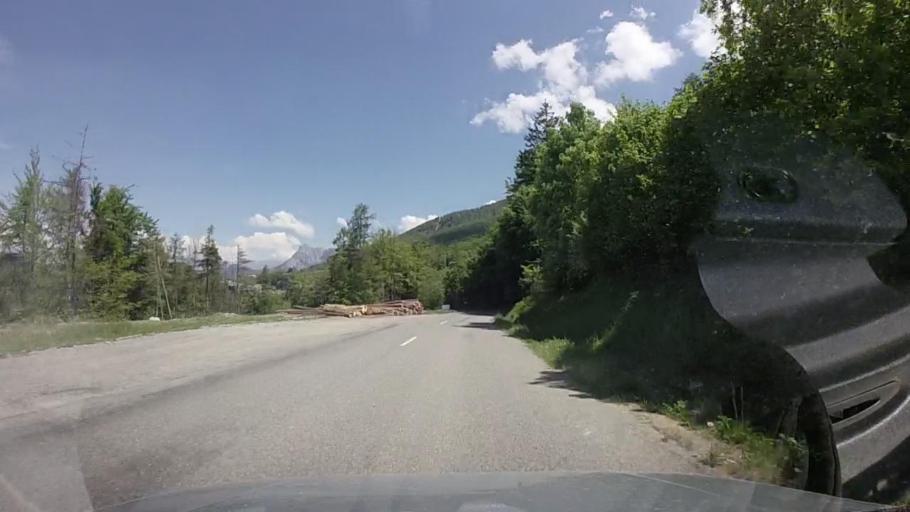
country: FR
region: Provence-Alpes-Cote d'Azur
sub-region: Departement des Alpes-de-Haute-Provence
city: Seyne-les-Alpes
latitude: 44.4069
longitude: 6.3492
